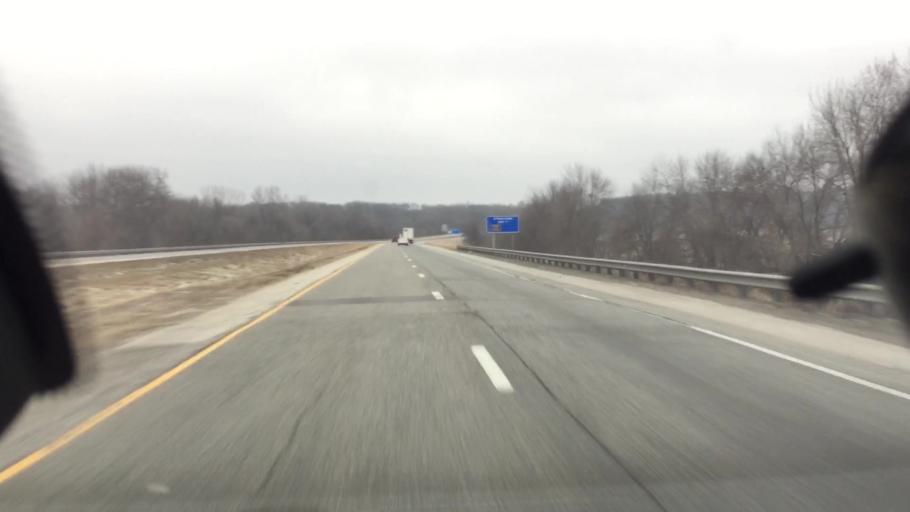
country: US
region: Illinois
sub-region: Henry County
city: Colona
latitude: 41.5098
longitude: -90.3406
